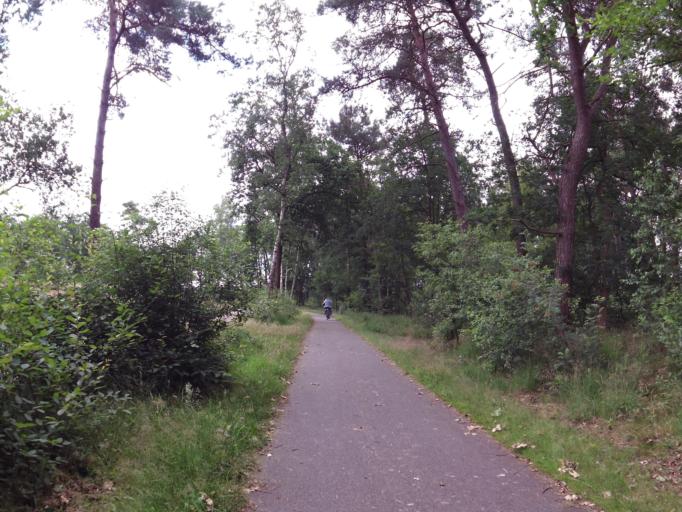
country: NL
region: North Brabant
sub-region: Gemeente Valkenswaard
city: Valkenswaard
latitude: 51.3289
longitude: 5.4457
